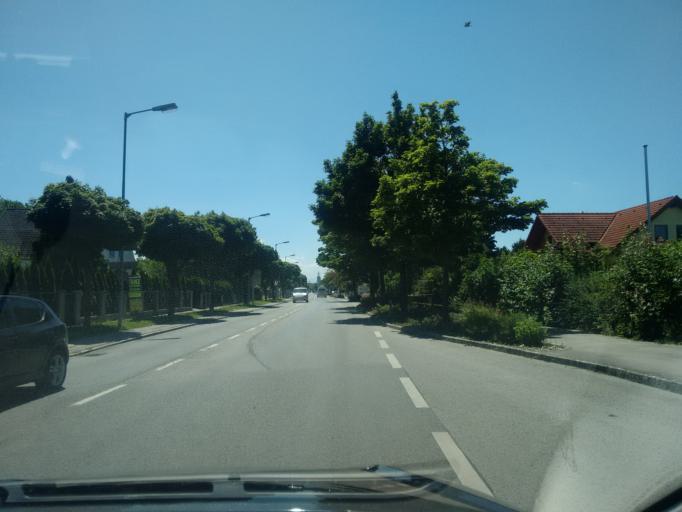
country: AT
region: Lower Austria
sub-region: Sankt Polten Stadt
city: Sankt Poelten
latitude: 48.2145
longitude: 15.6509
